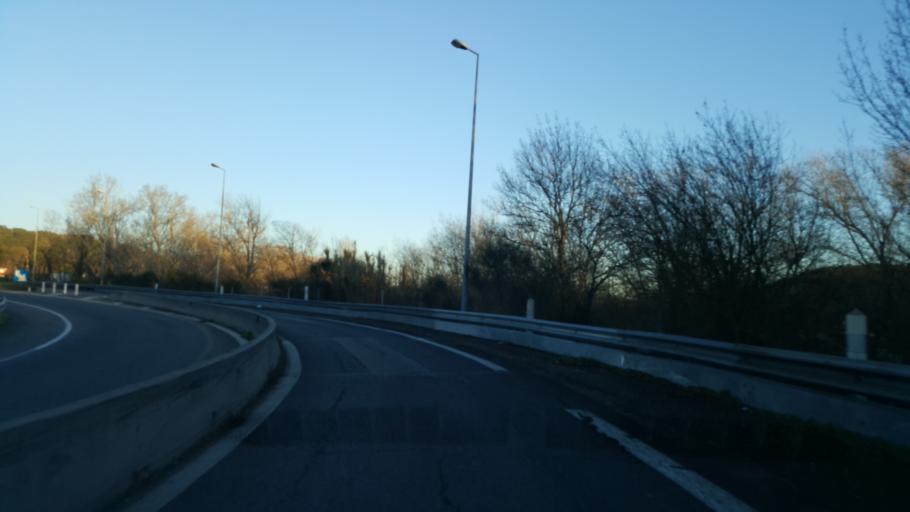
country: FR
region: Provence-Alpes-Cote d'Azur
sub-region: Departement des Bouches-du-Rhone
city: Aix-en-Provence
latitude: 43.5119
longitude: 5.4687
